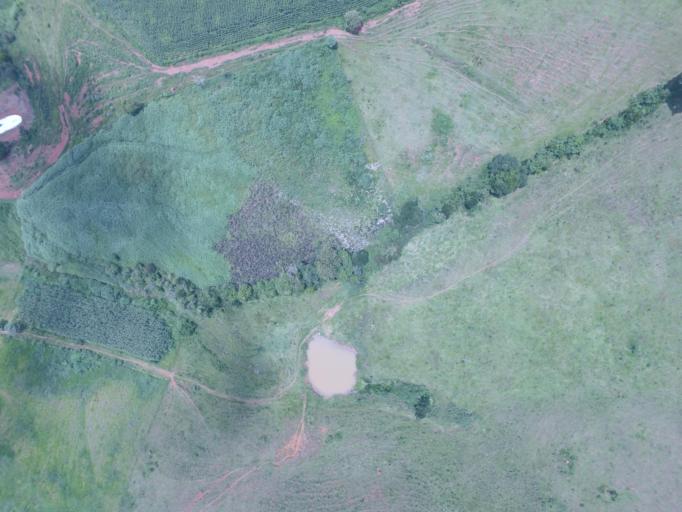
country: BR
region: Minas Gerais
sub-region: Tiradentes
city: Tiradentes
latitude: -21.0906
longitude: -44.0764
